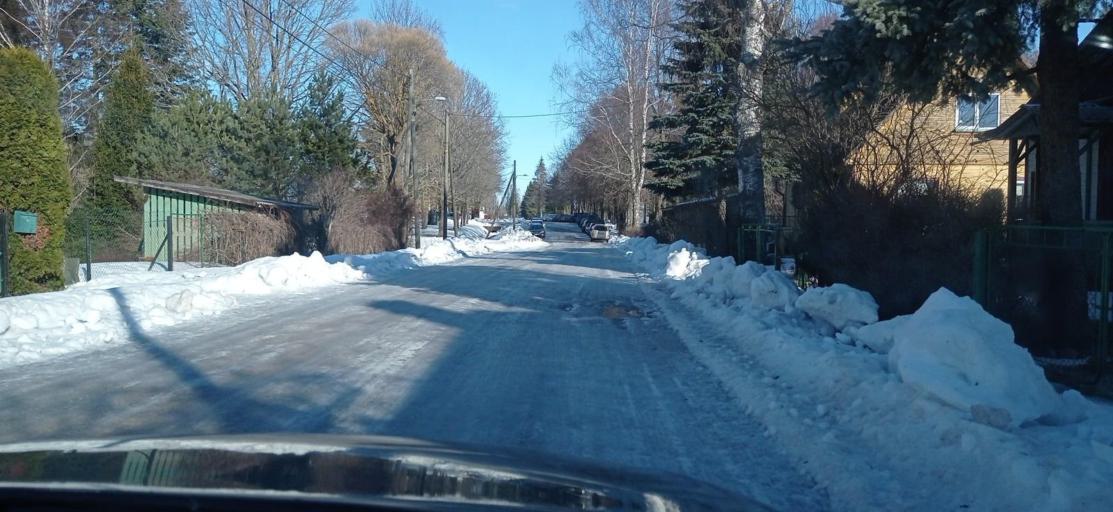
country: EE
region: Tartu
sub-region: Alatskivi vald
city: Kallaste
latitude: 58.6619
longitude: 27.1591
